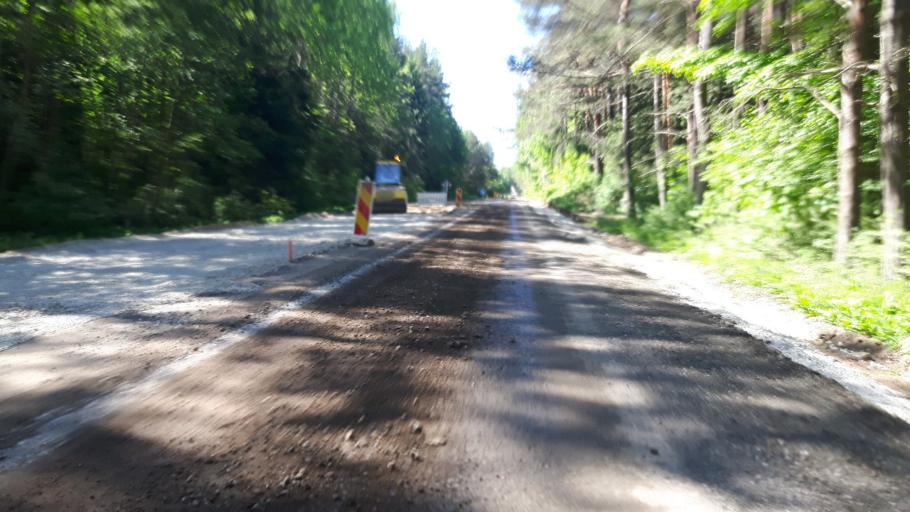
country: EE
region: Ida-Virumaa
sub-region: Narva-Joesuu linn
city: Narva-Joesuu
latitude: 59.4216
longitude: 27.9781
